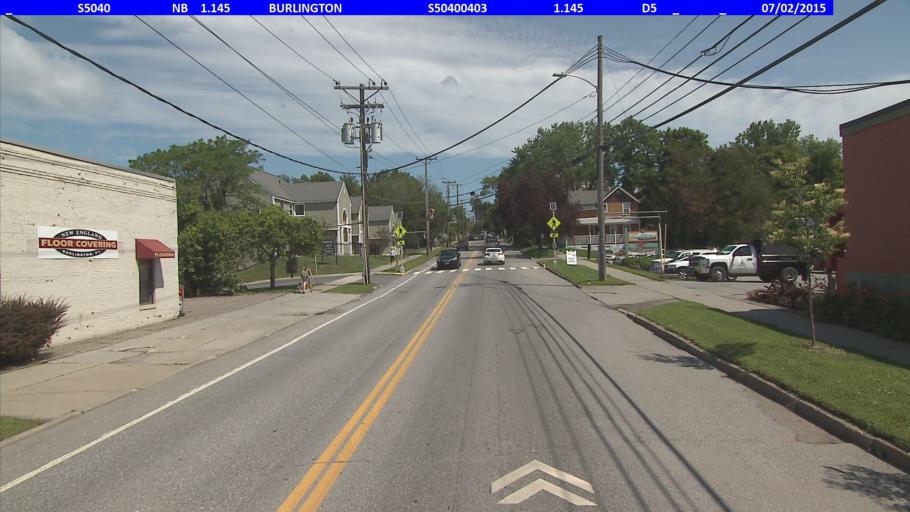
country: US
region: Vermont
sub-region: Chittenden County
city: Burlington
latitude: 44.4719
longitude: -73.2153
